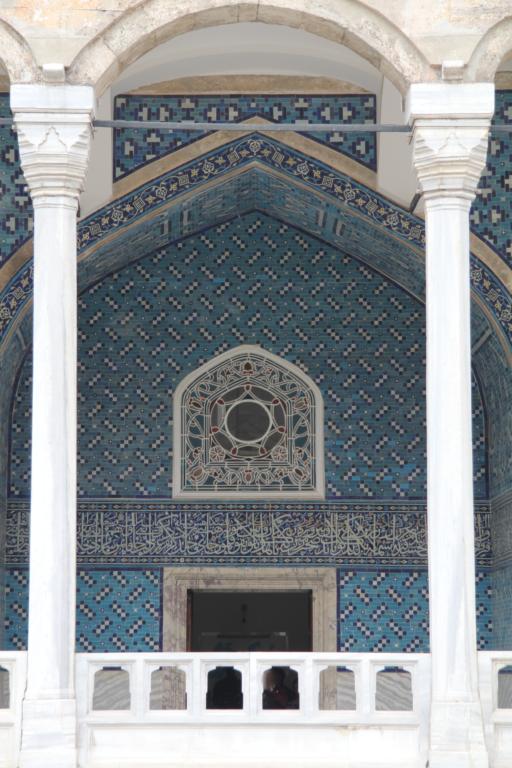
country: TR
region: Istanbul
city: Eminoenue
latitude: 41.0120
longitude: 28.9813
